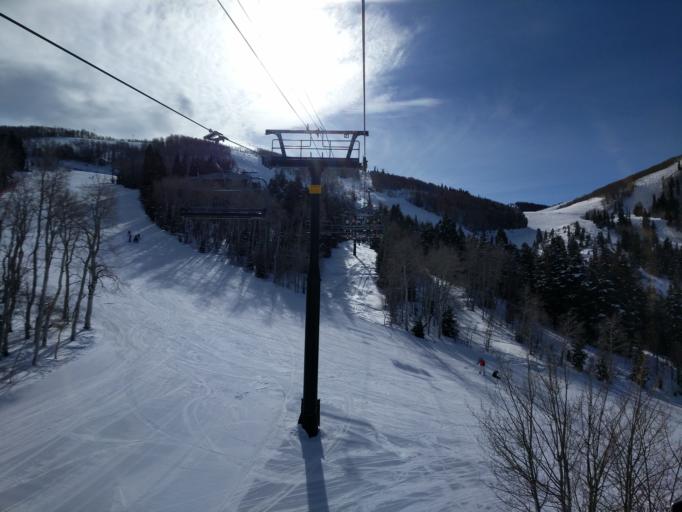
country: US
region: Utah
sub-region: Summit County
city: Park City
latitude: 40.6431
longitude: -111.5081
